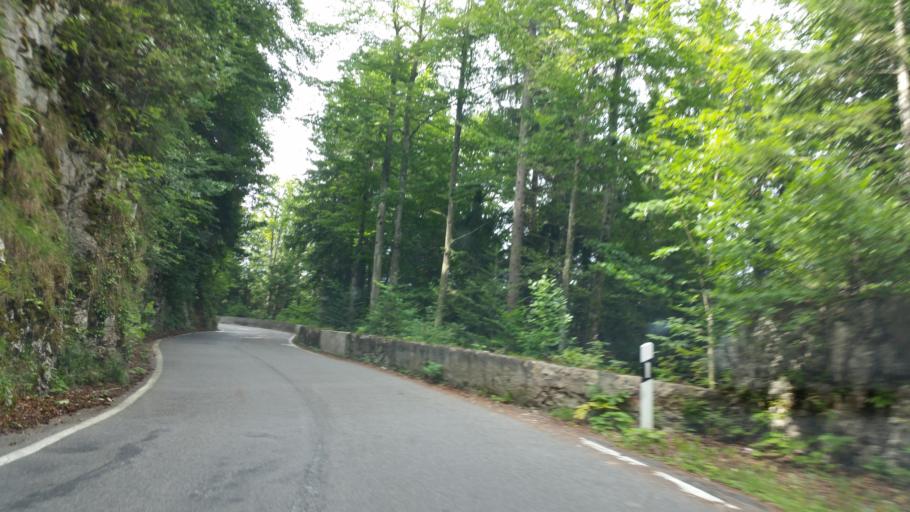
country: CH
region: Neuchatel
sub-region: La Chaux-de-Fonds District
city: La Chaux-de-Fonds
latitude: 47.1313
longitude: 6.8255
